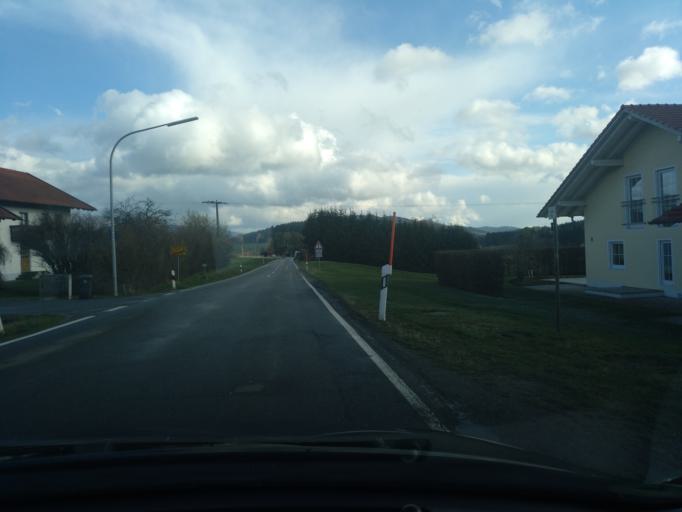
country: DE
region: Bavaria
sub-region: Lower Bavaria
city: Konzell
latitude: 49.1022
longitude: 12.7205
